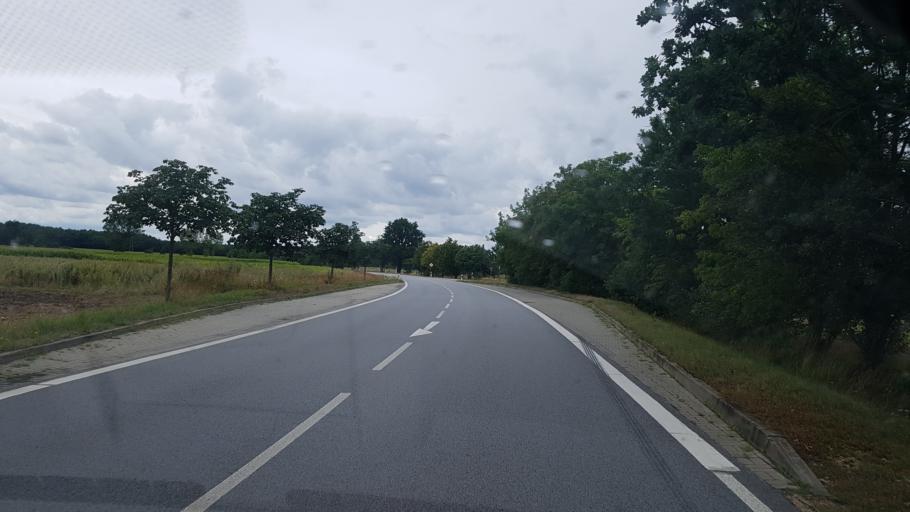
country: DE
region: Saxony
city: Niesky
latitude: 51.2582
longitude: 14.8095
